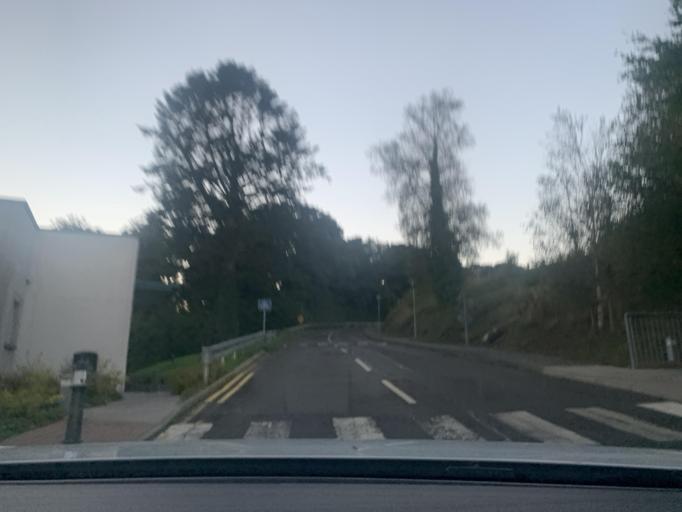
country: IE
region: Connaught
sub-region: Sligo
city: Sligo
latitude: 54.2593
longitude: -8.3843
